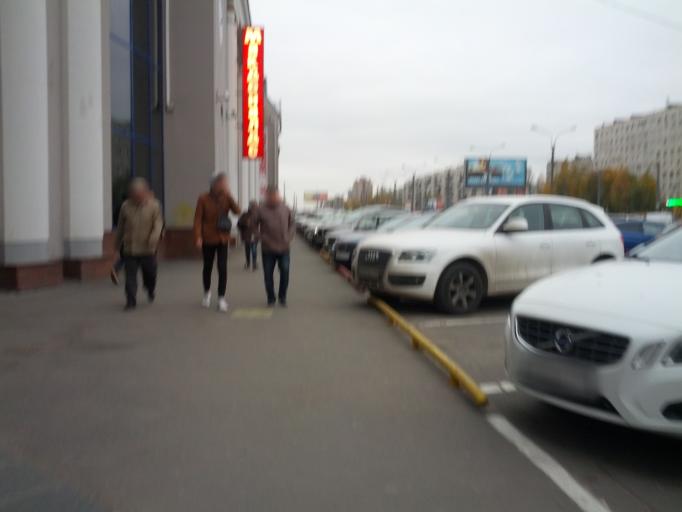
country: RU
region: St.-Petersburg
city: Krasnogvargeisky
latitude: 59.9089
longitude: 30.4817
